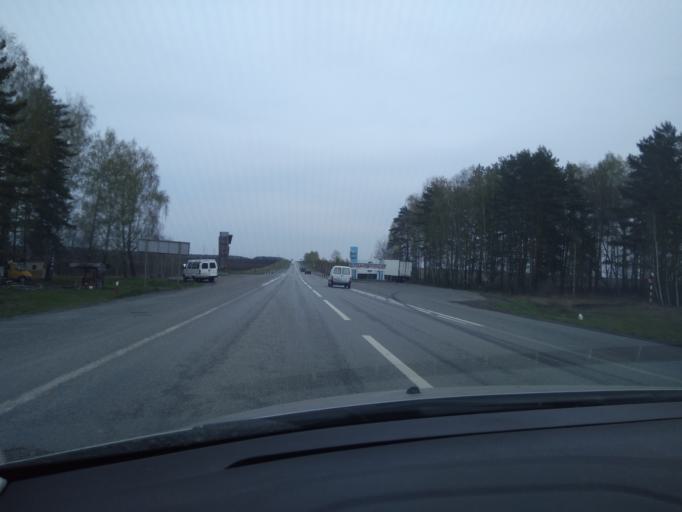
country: RU
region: Sverdlovsk
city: Gryaznovskoye
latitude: 56.7794
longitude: 61.5884
